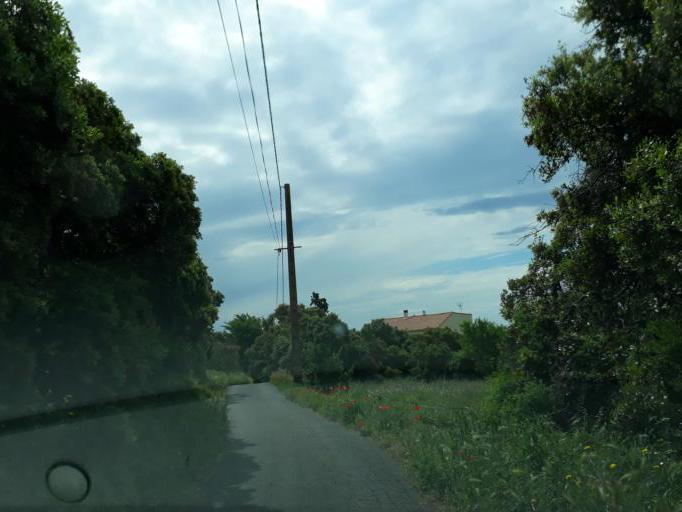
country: FR
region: Languedoc-Roussillon
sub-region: Departement de l'Herault
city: Agde
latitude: 43.2942
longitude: 3.4898
